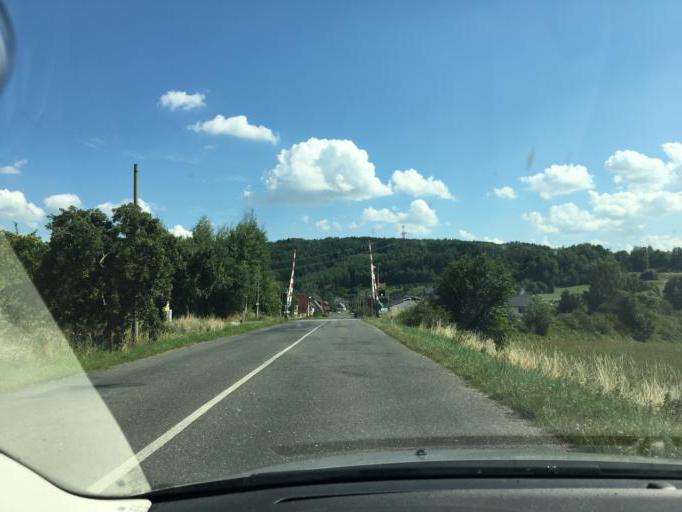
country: CZ
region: Liberecky
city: Hodkovice nad Mohelkou
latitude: 50.6574
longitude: 15.1040
